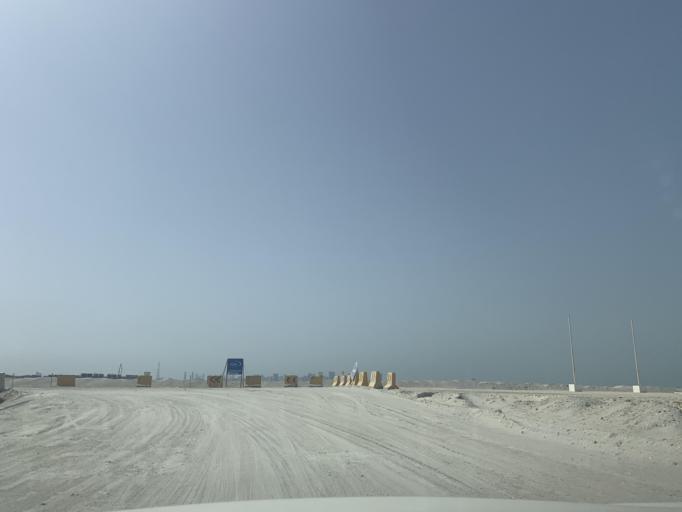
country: BH
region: Northern
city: Sitrah
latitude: 26.1608
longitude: 50.6417
